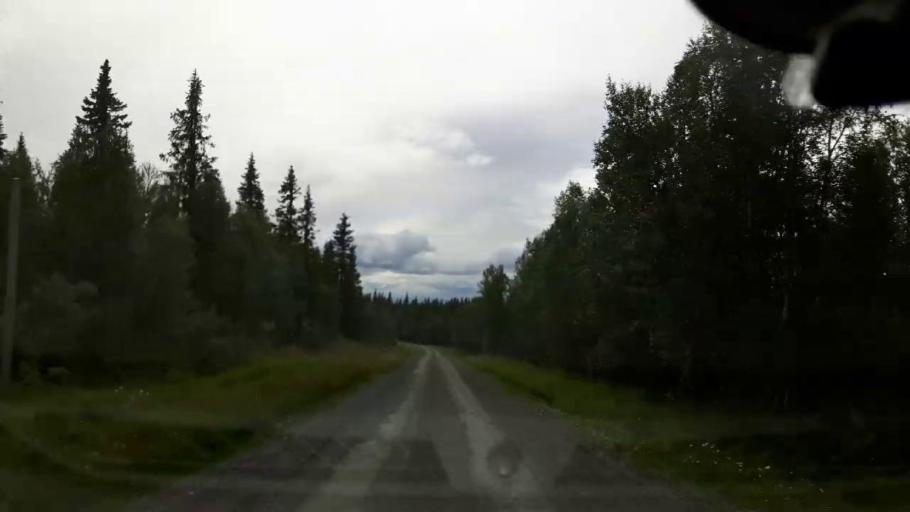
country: SE
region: Jaemtland
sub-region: Krokoms Kommun
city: Valla
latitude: 63.7607
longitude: 13.8370
